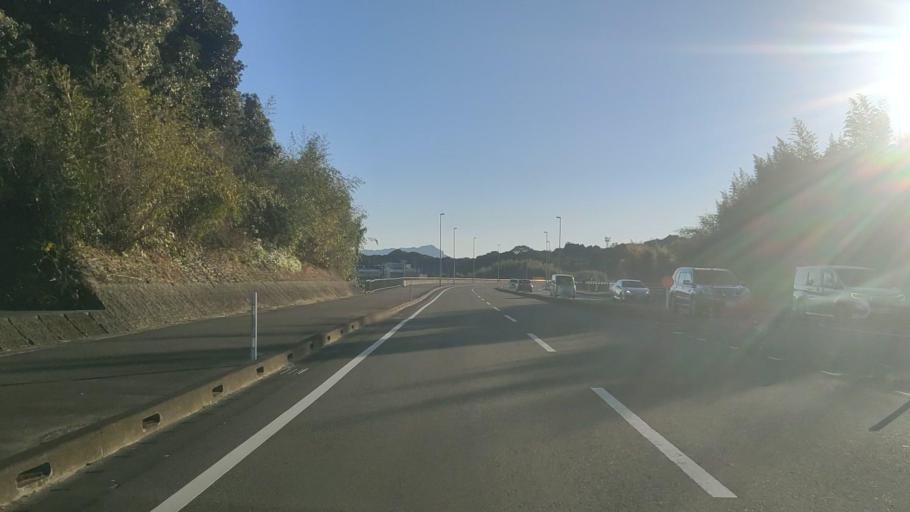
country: JP
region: Miyazaki
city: Miyazaki-shi
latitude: 31.8887
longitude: 131.4028
